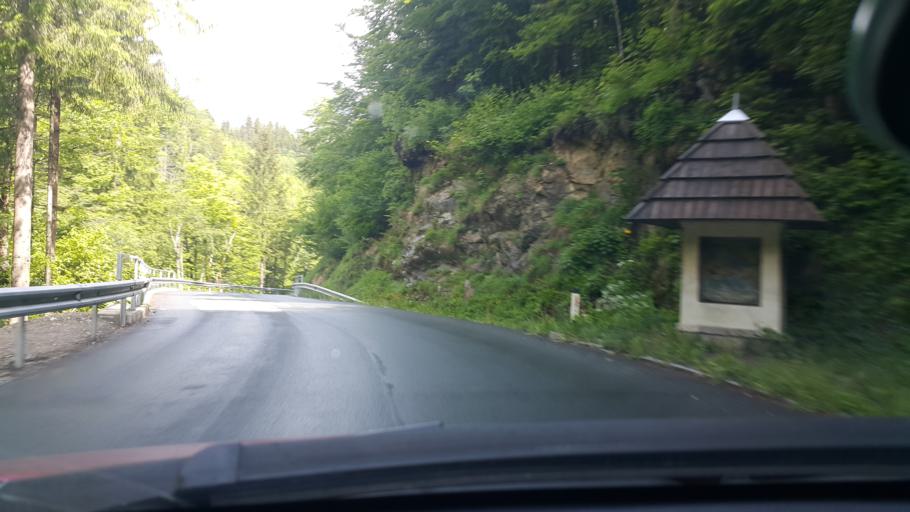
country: AT
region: Carinthia
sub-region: Politischer Bezirk Klagenfurt Land
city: Ferlach
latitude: 46.4680
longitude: 14.2584
